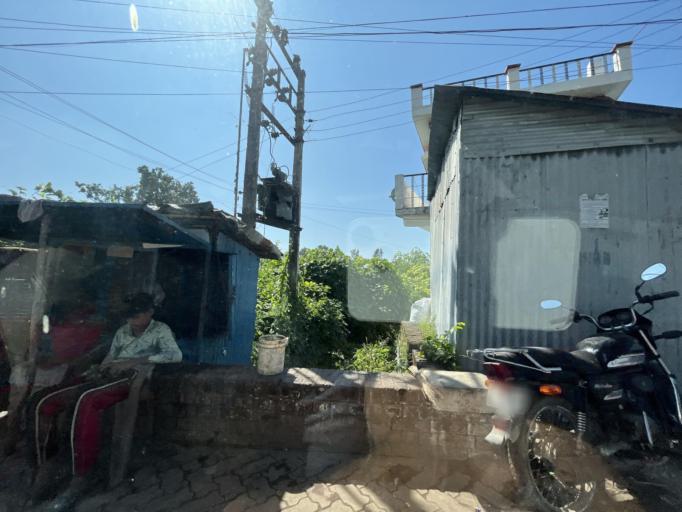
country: IN
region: Uttarakhand
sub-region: Naini Tal
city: Haldwani
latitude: 29.2102
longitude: 79.4644
